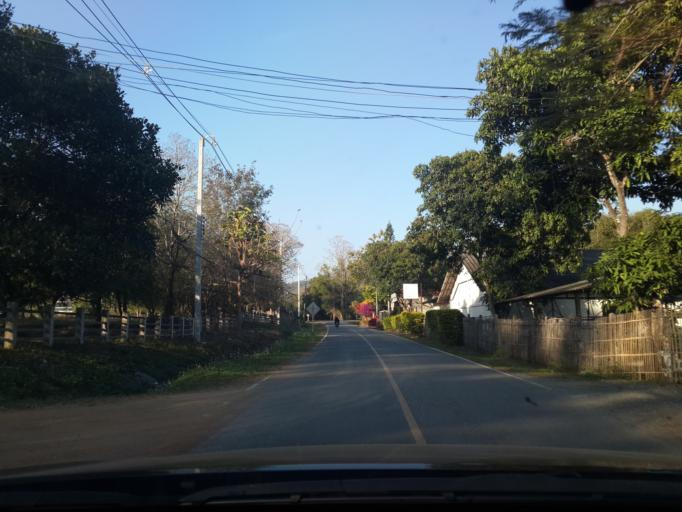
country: TH
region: Chiang Mai
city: San Sai
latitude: 18.9239
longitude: 99.1381
